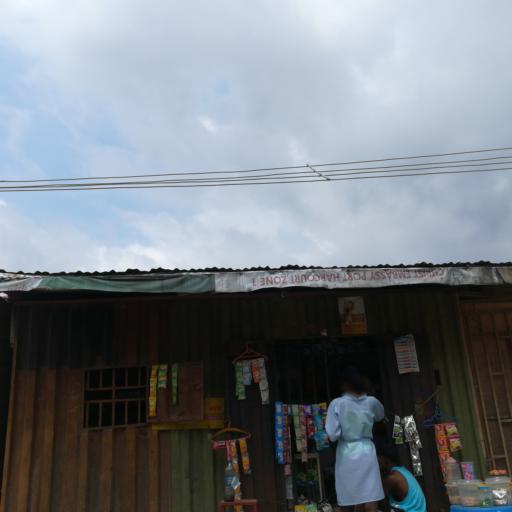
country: NG
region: Rivers
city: Port Harcourt
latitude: 4.8394
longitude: 7.0769
